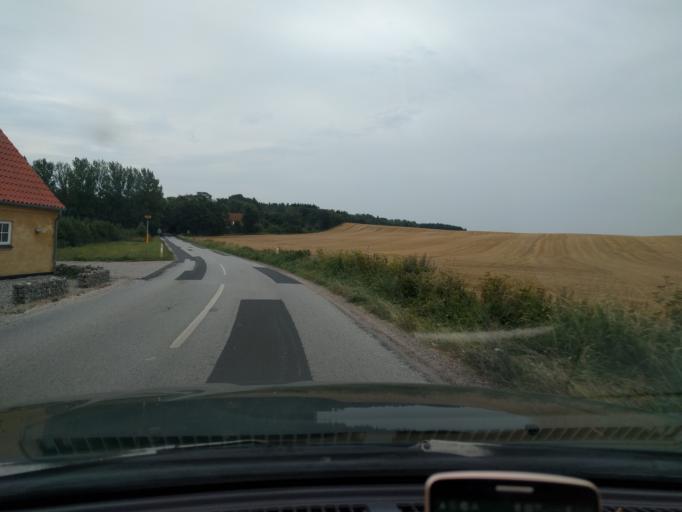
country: DK
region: Zealand
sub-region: Slagelse Kommune
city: Skaelskor
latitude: 55.2842
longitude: 11.2684
